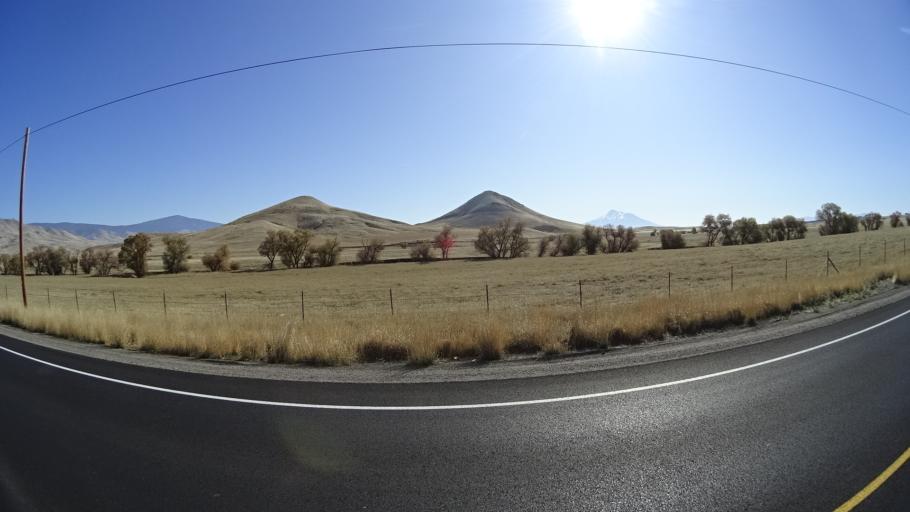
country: US
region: California
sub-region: Siskiyou County
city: Montague
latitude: 41.8328
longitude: -122.4885
